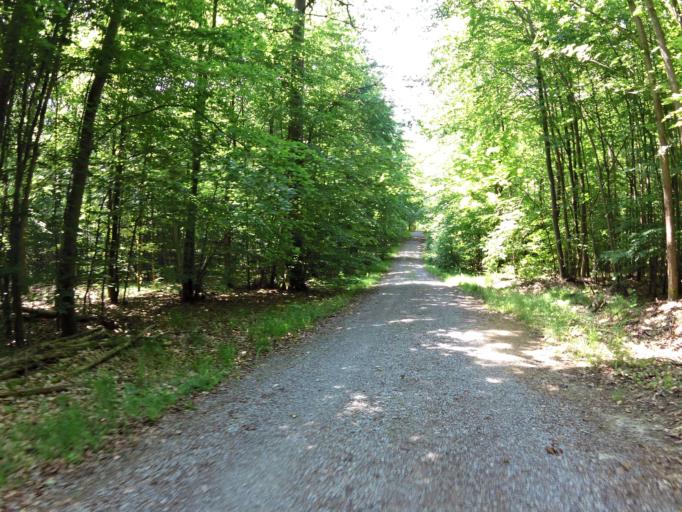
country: DE
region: Bavaria
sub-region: Regierungsbezirk Unterfranken
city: Kist
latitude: 49.7278
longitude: 9.8665
